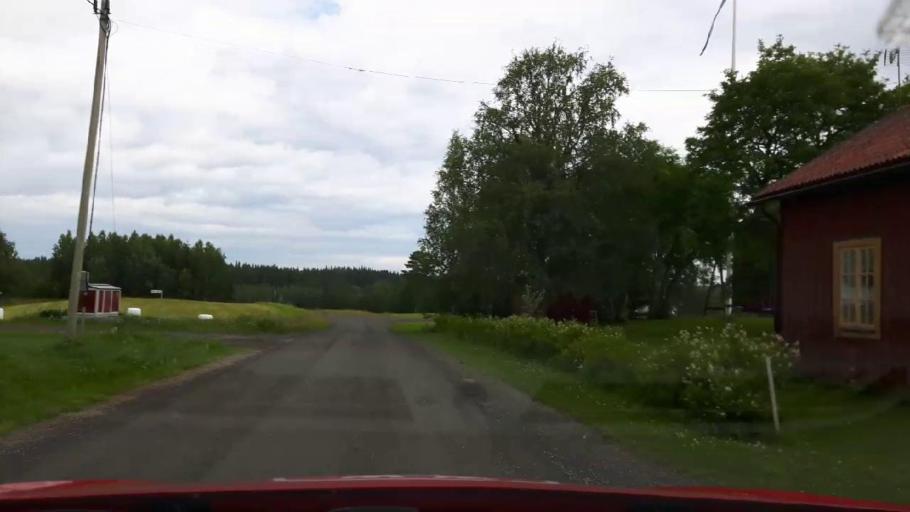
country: SE
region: Jaemtland
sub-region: Stroemsunds Kommun
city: Stroemsund
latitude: 63.4574
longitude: 15.2800
